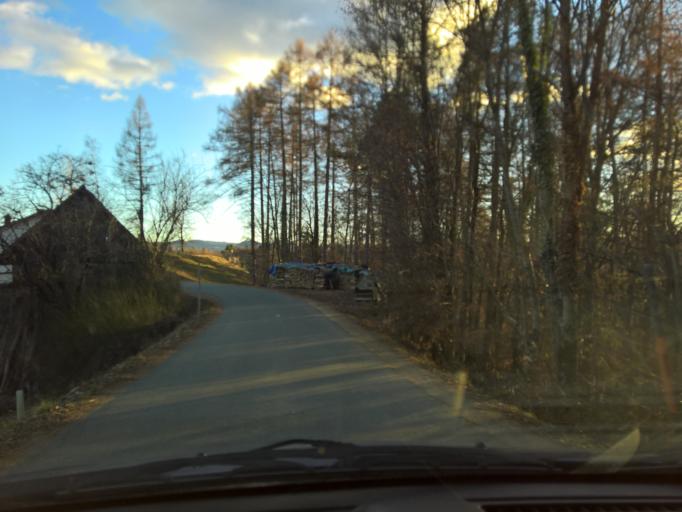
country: AT
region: Styria
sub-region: Politischer Bezirk Leibnitz
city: Leutschach
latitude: 46.6933
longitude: 15.4414
